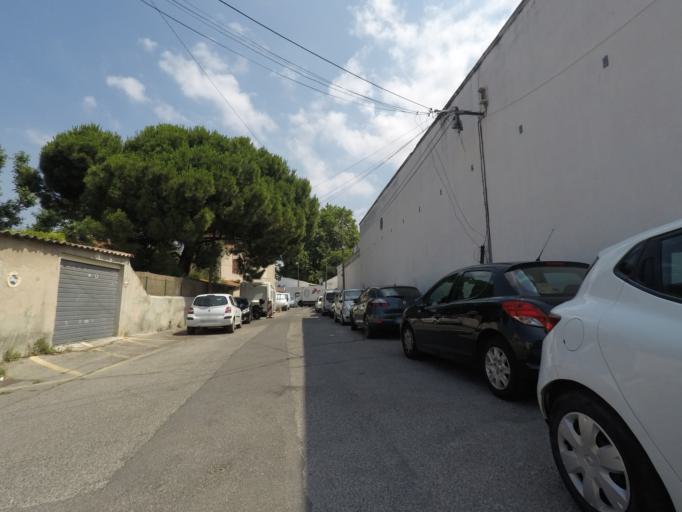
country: FR
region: Provence-Alpes-Cote d'Azur
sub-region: Departement des Bouches-du-Rhone
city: Marseille 10
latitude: 43.2775
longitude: 5.4115
